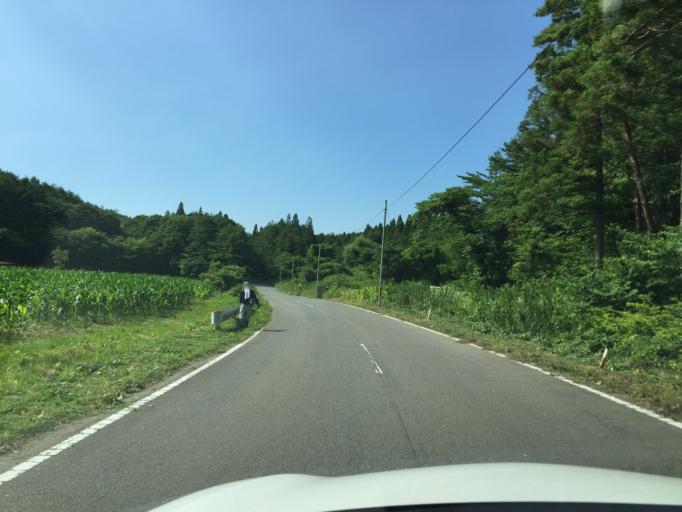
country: JP
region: Fukushima
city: Ishikawa
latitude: 37.1525
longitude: 140.6334
